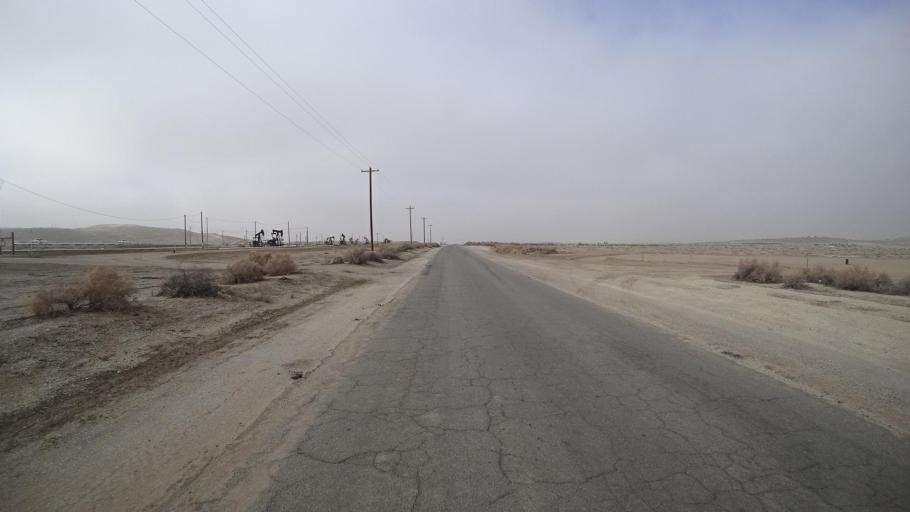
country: US
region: California
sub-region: Kern County
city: Maricopa
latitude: 35.0353
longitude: -119.3542
